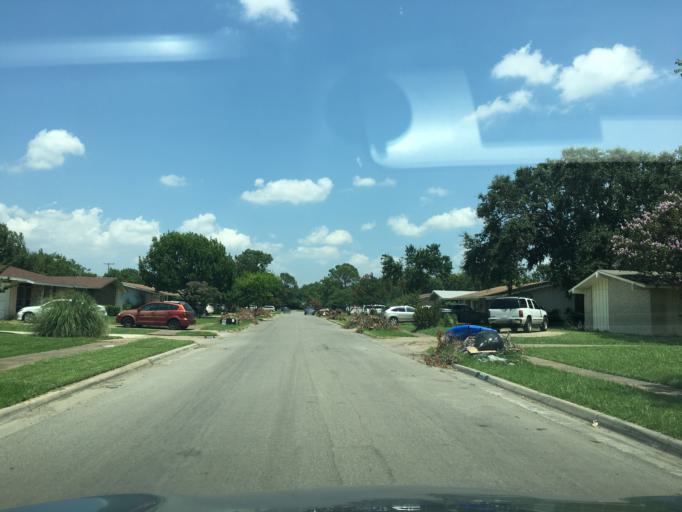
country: US
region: Texas
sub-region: Dallas County
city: Farmers Branch
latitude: 32.9123
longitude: -96.8683
